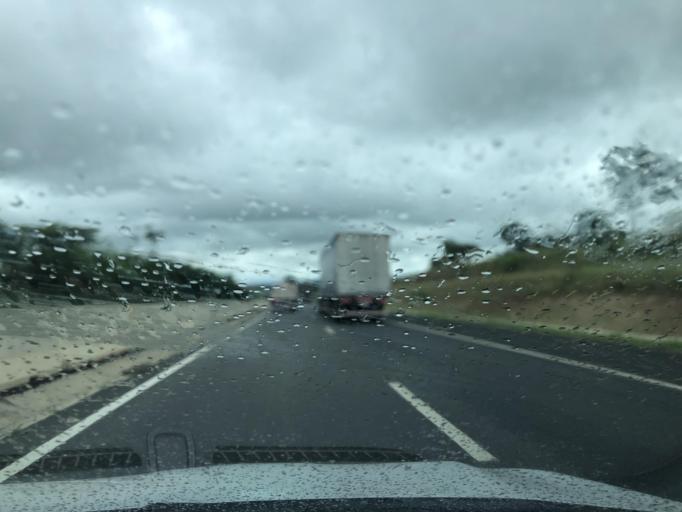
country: BR
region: Goias
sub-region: Catalao
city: Catalao
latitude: -18.2633
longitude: -47.9996
